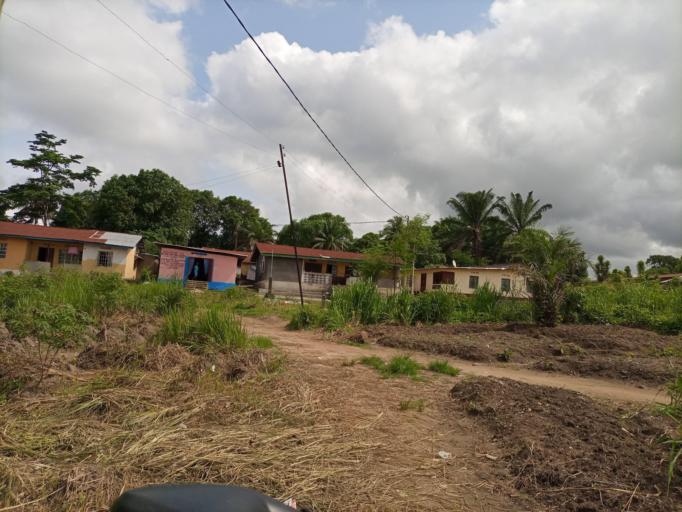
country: SL
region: Southern Province
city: Bo
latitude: 7.9636
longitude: -11.7617
